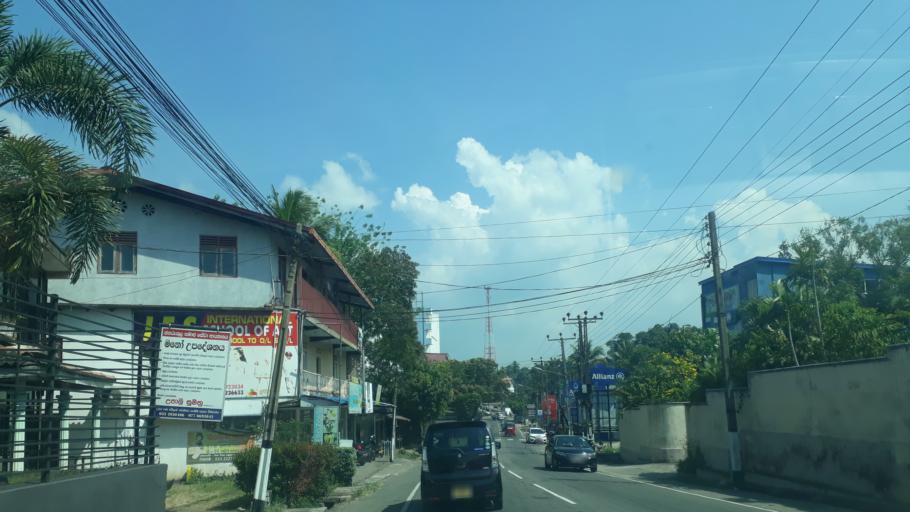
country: LK
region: Western
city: Gampaha
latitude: 7.0893
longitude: 80.0048
